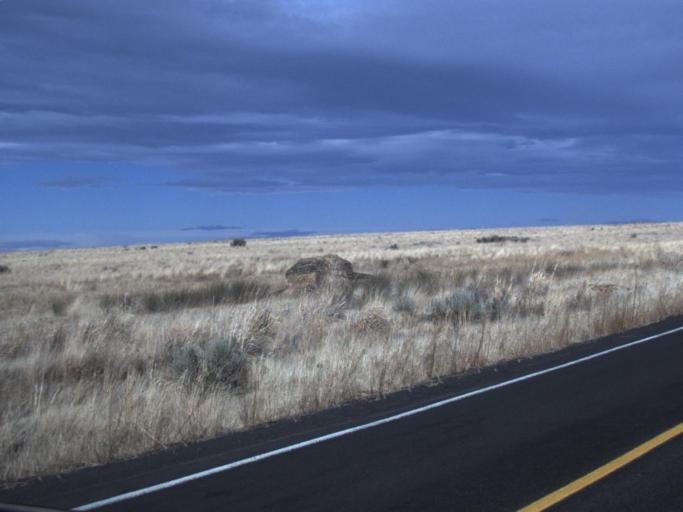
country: US
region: Washington
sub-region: Adams County
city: Ritzville
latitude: 47.3134
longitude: -118.6904
